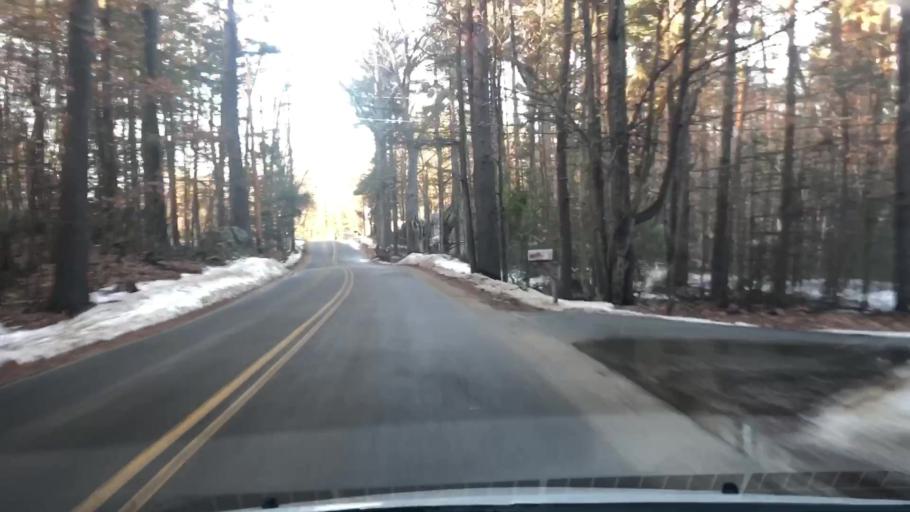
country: US
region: New Hampshire
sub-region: Hillsborough County
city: Milford
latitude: 42.8036
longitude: -71.6466
